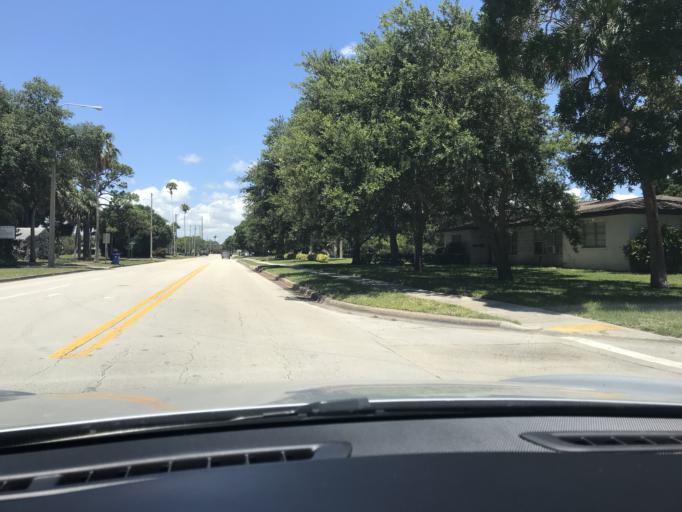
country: US
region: Florida
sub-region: Indian River County
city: Vero Beach
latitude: 27.6420
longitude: -80.3946
